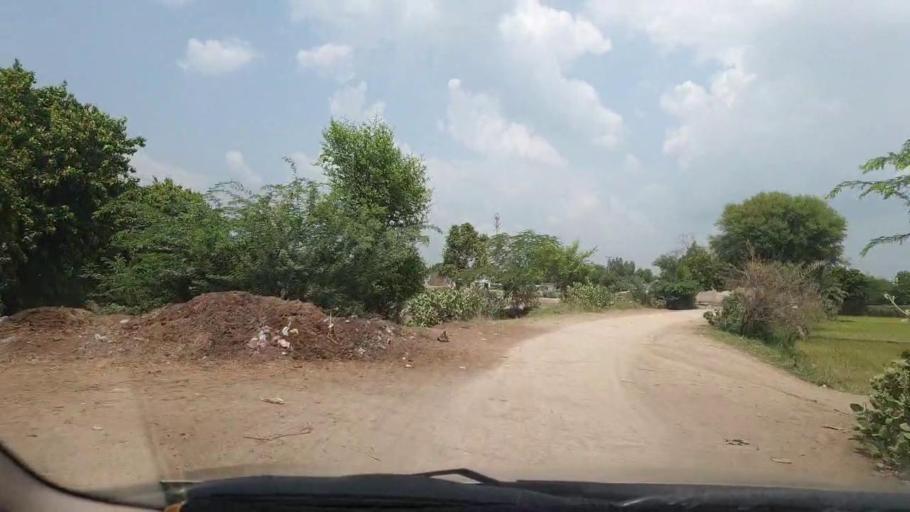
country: PK
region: Sindh
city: Larkana
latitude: 27.5755
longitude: 68.1219
